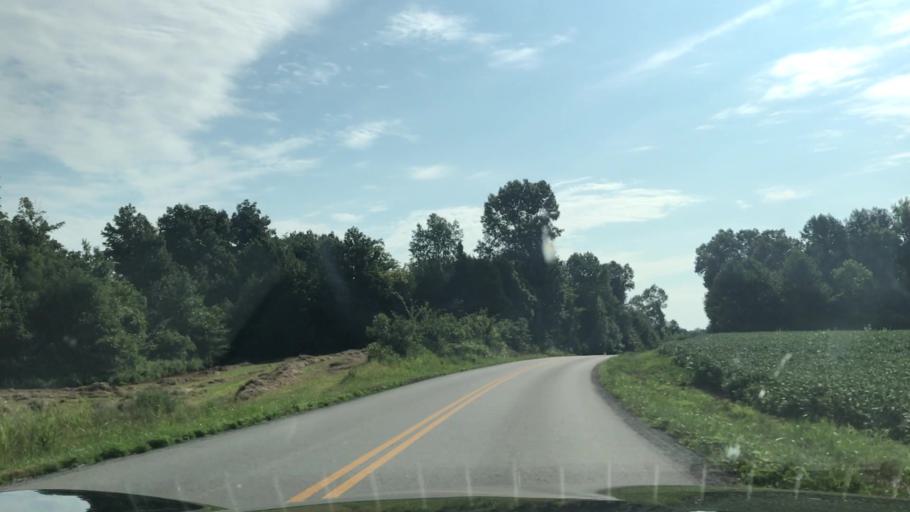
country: US
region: Kentucky
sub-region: Green County
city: Greensburg
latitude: 37.2256
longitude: -85.6603
